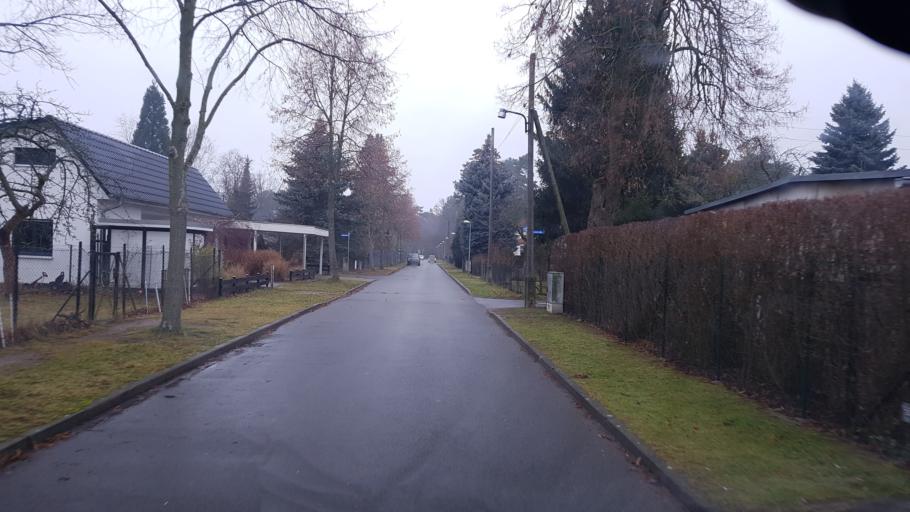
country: DE
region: Brandenburg
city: Stahnsdorf
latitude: 52.3764
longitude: 13.2141
